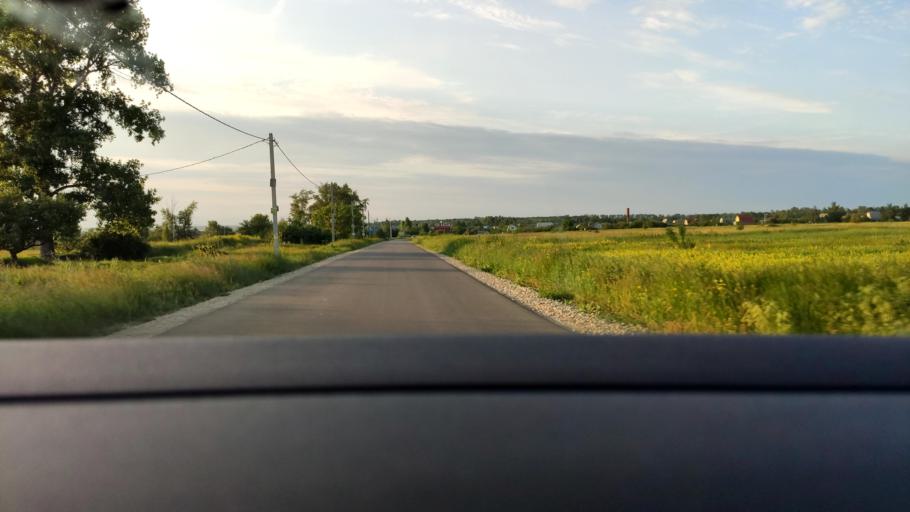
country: RU
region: Voronezj
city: Podgornoye
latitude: 51.8945
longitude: 39.1756
